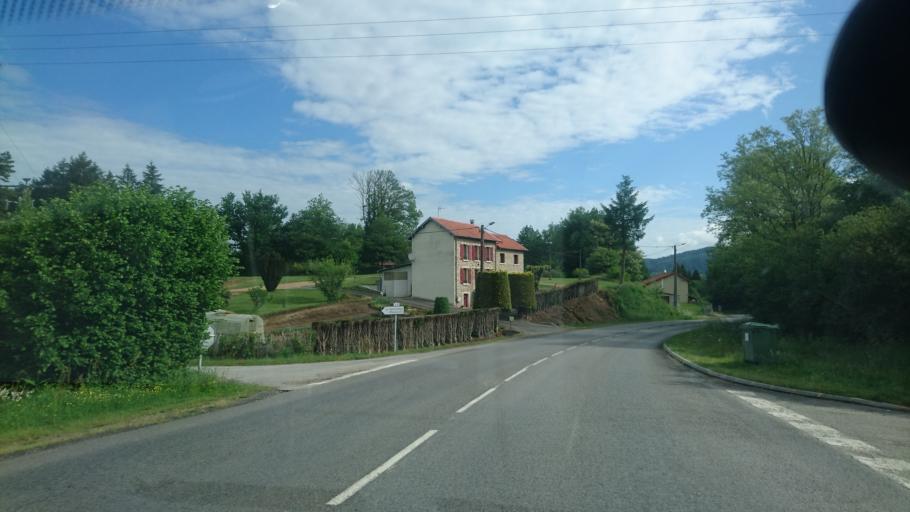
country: FR
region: Limousin
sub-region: Departement de la Haute-Vienne
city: Peyrat-le-Chateau
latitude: 45.8003
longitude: 1.7638
